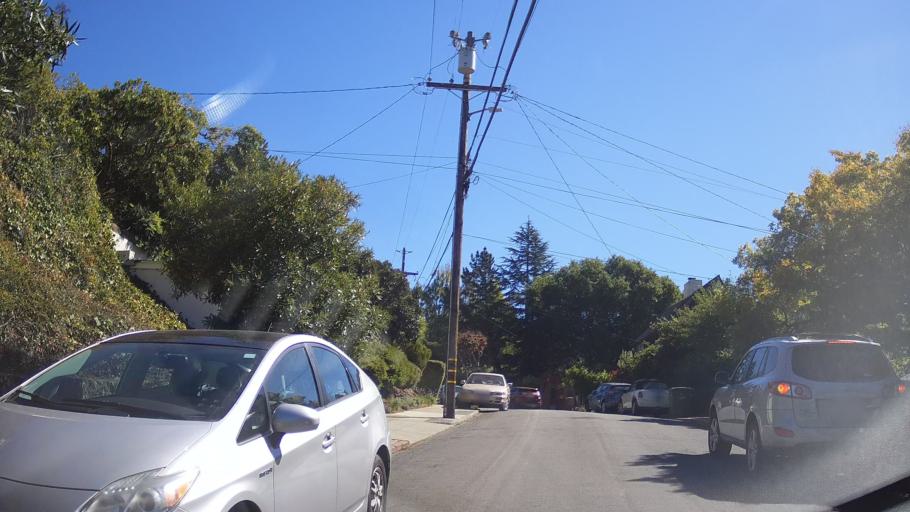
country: US
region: California
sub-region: Alameda County
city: Berkeley
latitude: 37.8909
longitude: -122.2657
